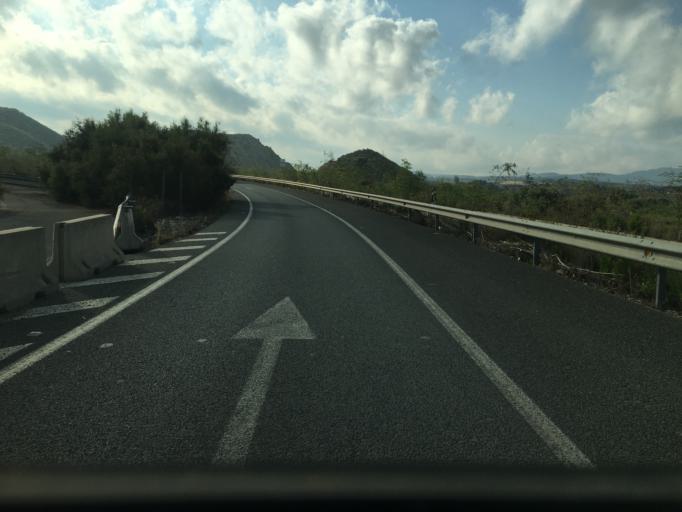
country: ES
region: Murcia
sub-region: Murcia
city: Beniel
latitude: 38.0015
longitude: -1.0137
